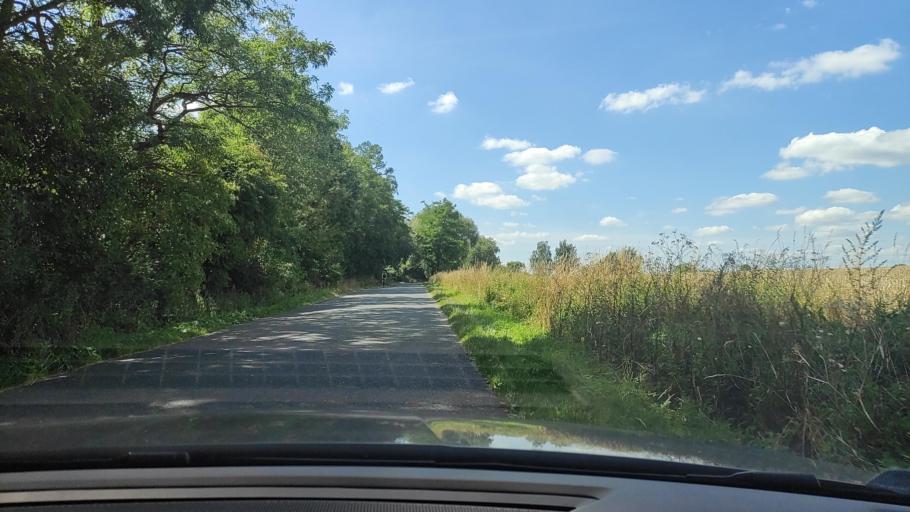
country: PL
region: Greater Poland Voivodeship
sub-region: Powiat poznanski
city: Kobylnica
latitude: 52.4851
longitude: 17.1392
